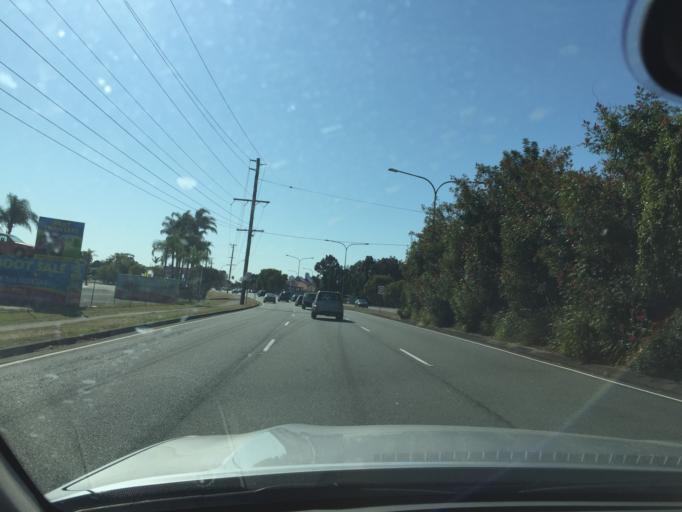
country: AU
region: Queensland
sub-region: Gold Coast
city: Clear Island Waters
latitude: -28.0321
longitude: 153.3894
